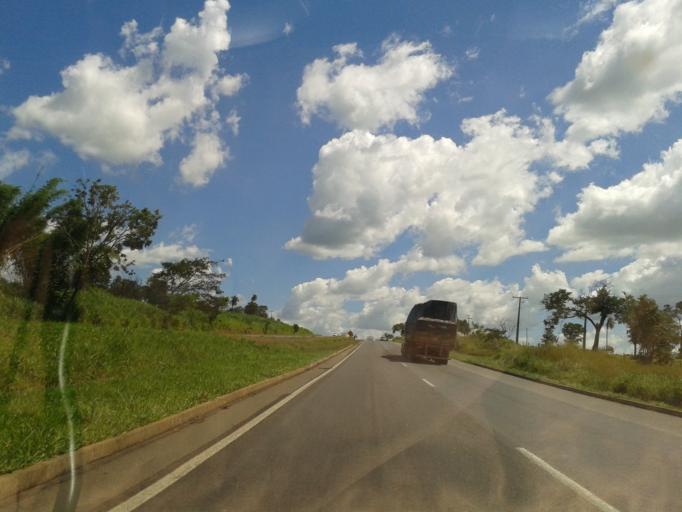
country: BR
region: Goias
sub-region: Piracanjuba
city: Piracanjuba
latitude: -17.3576
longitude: -49.2481
